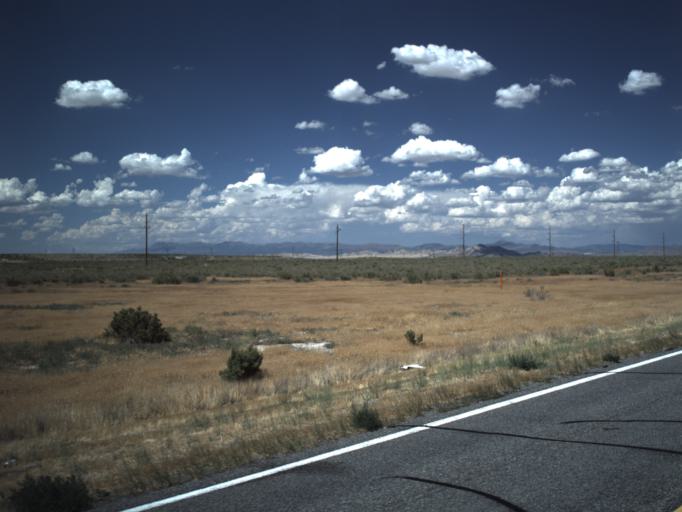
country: US
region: Utah
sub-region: Millard County
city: Delta
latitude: 39.4647
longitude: -112.4302
